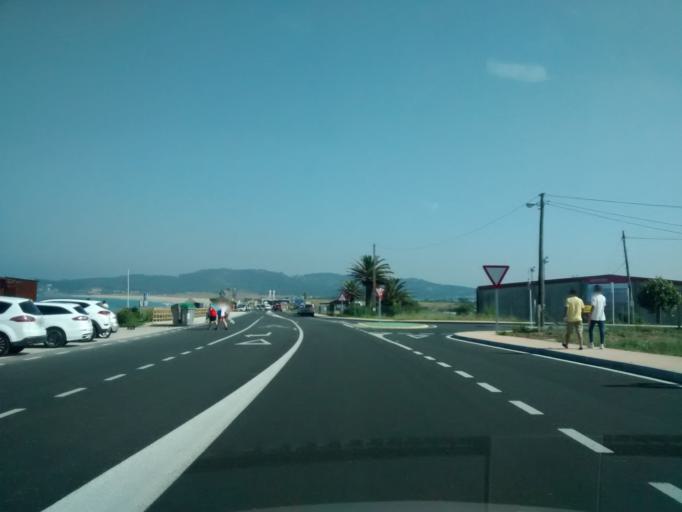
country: ES
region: Galicia
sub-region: Provincia de Pontevedra
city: O Grove
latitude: 42.4369
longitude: -8.8705
